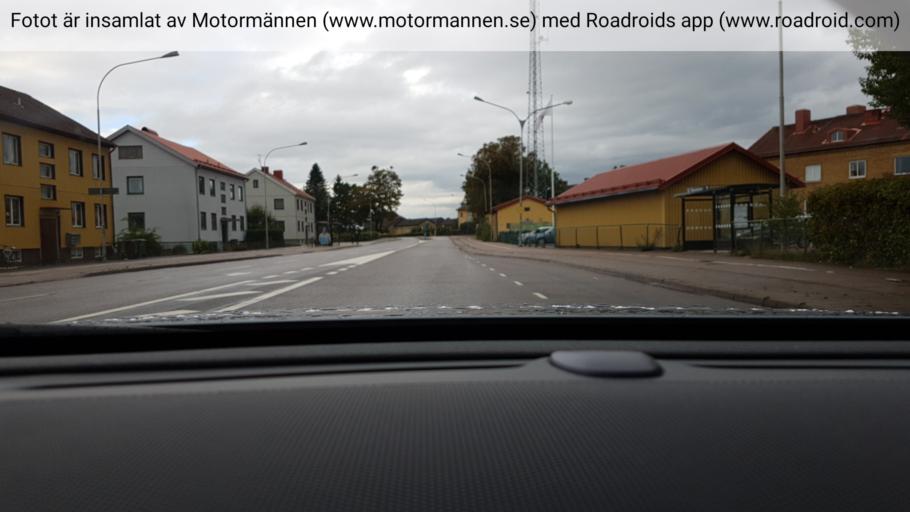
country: SE
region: Vaestra Goetaland
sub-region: Vanersborgs Kommun
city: Vanersborg
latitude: 58.3695
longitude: 12.3230
